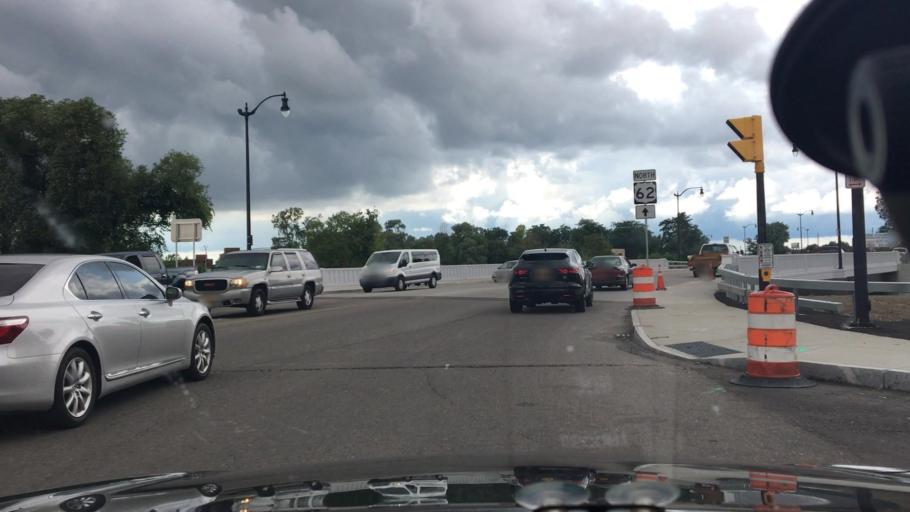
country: US
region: New York
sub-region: Erie County
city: West Seneca
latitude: 42.8600
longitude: -78.8255
